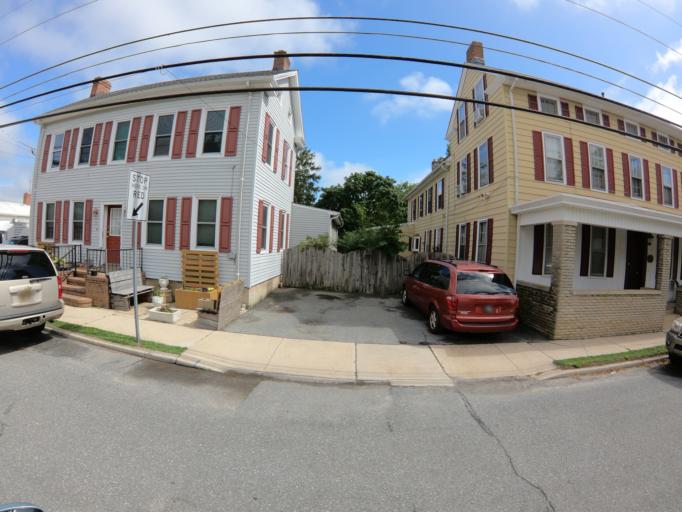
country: US
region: Delaware
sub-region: Kent County
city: Felton
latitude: 39.0082
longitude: -75.5750
